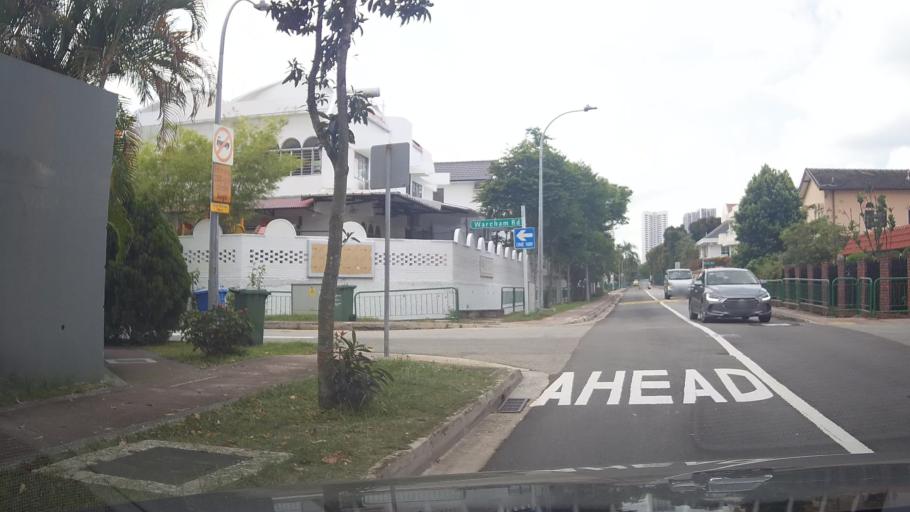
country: SG
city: Singapore
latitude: 1.3079
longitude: 103.8929
